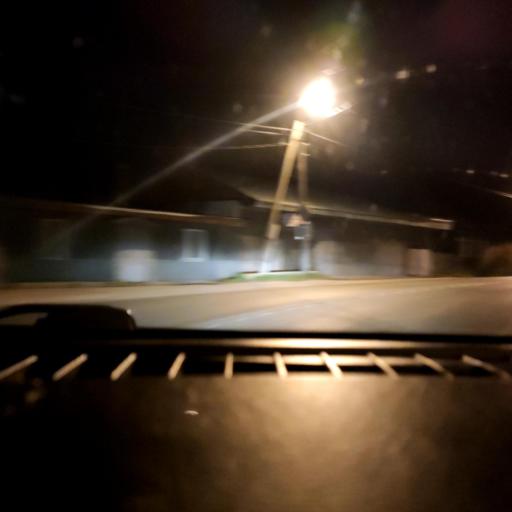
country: RU
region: Perm
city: Perm
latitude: 58.0361
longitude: 56.3370
